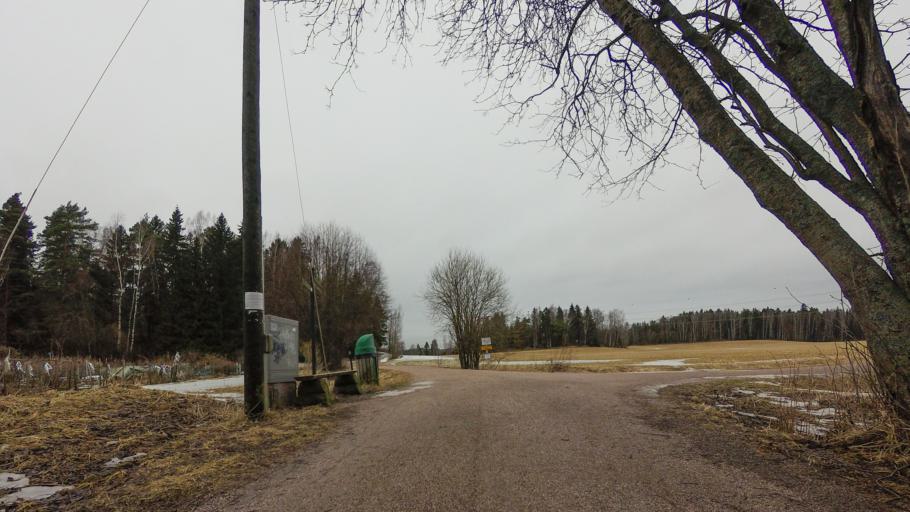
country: FI
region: Uusimaa
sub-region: Helsinki
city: Vantaa
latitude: 60.2112
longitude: 25.0284
